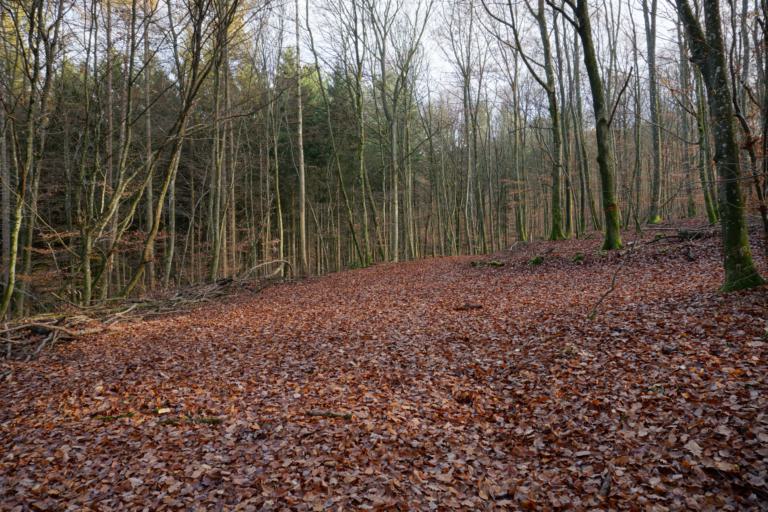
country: DE
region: Baden-Wuerttemberg
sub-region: Karlsruhe Region
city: Binau
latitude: 49.3250
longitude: 9.0326
